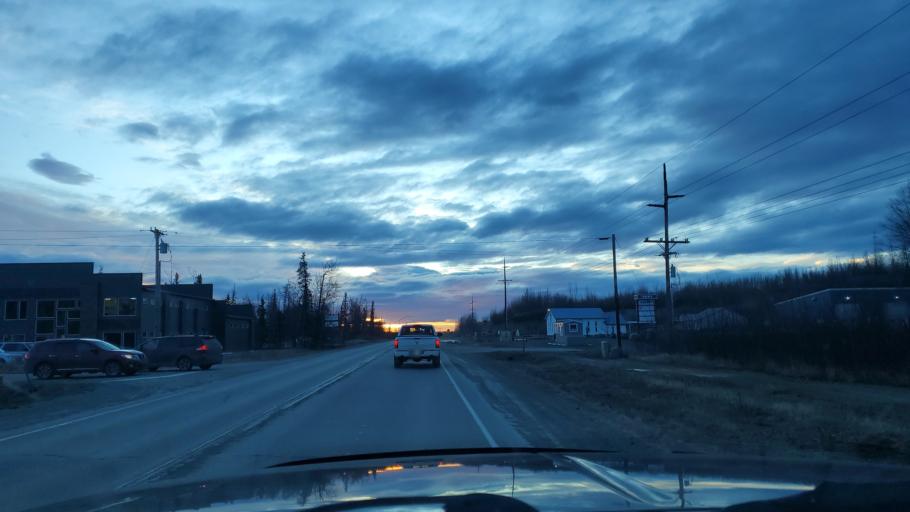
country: US
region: Alaska
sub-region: Matanuska-Susitna Borough
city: Lakes
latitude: 61.6027
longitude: -149.3543
